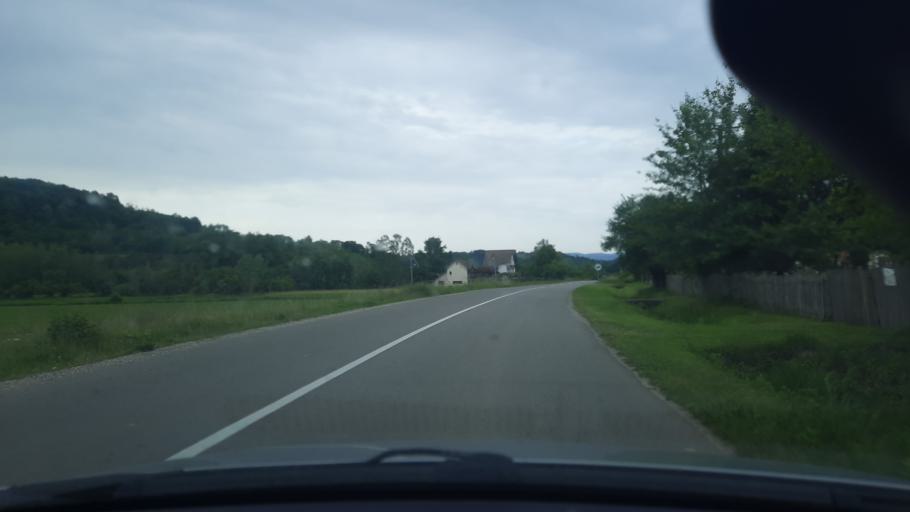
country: RS
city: Jarebice
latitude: 44.4947
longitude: 19.4867
